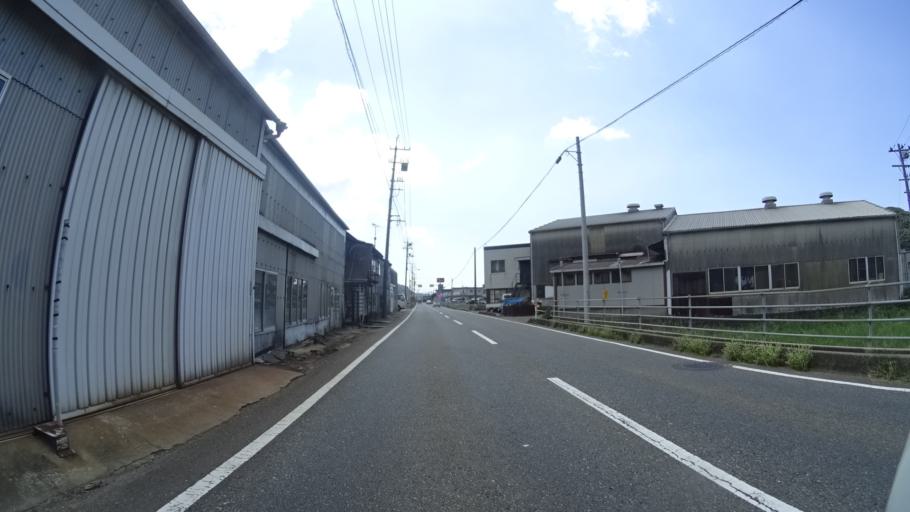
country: JP
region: Yamaguchi
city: Shimonoseki
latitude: 34.0774
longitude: 130.8960
